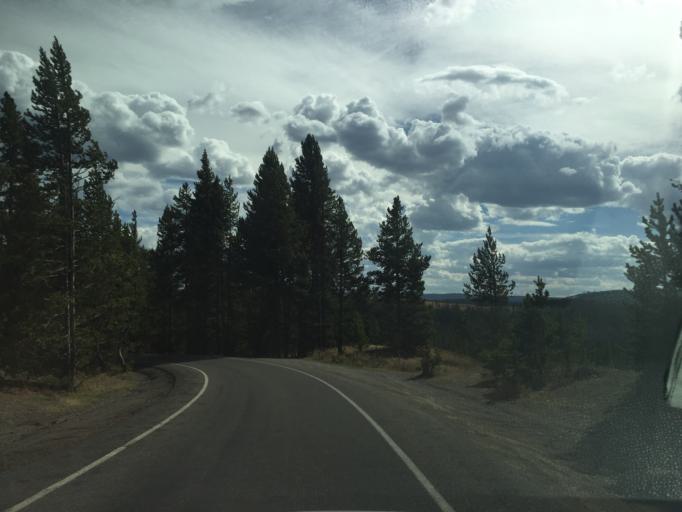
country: US
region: Montana
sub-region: Gallatin County
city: West Yellowstone
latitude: 44.7202
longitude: -110.4995
